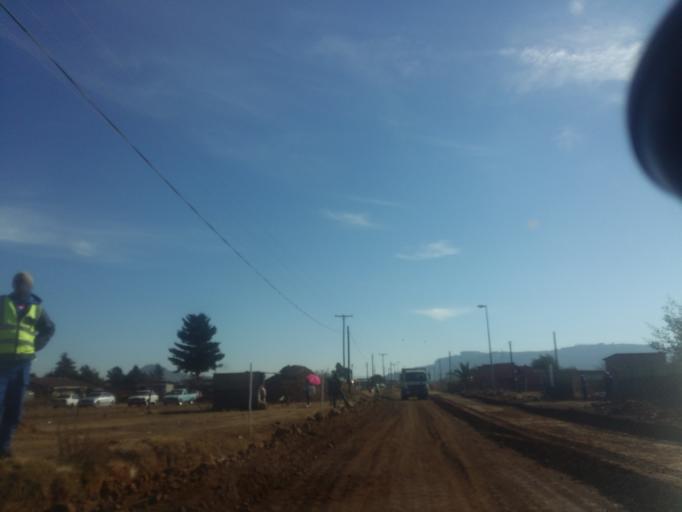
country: LS
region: Maseru
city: Maseru
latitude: -29.3701
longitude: 27.5267
